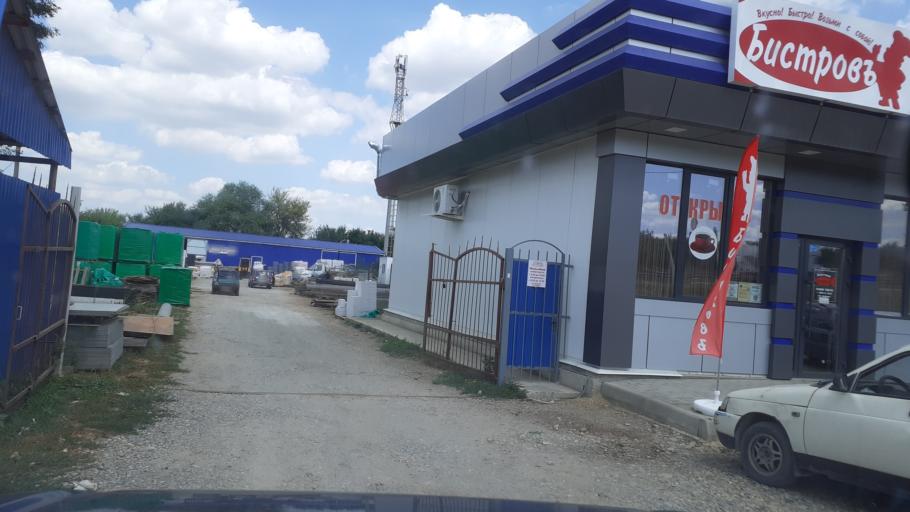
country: RU
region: Krasnodarskiy
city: Il'skiy
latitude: 44.8529
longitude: 38.5915
